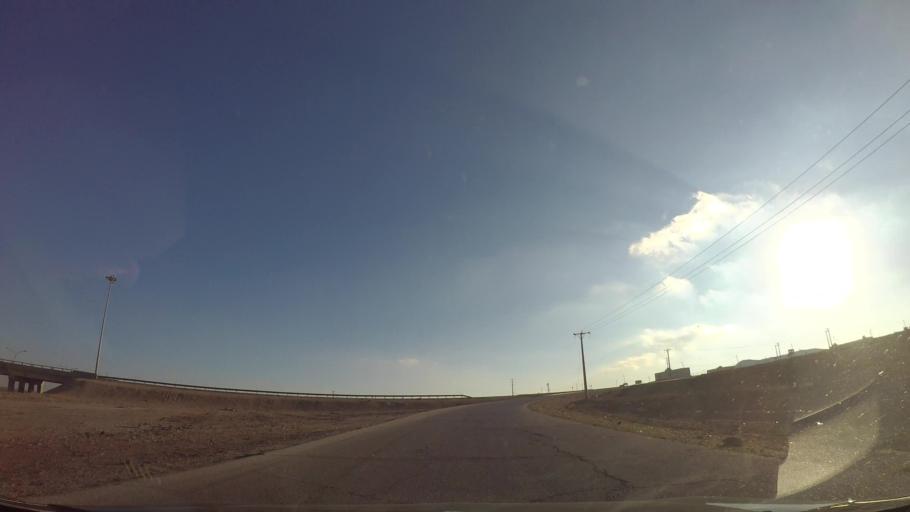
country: JO
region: Tafielah
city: Busayra
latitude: 30.4995
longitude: 35.7990
